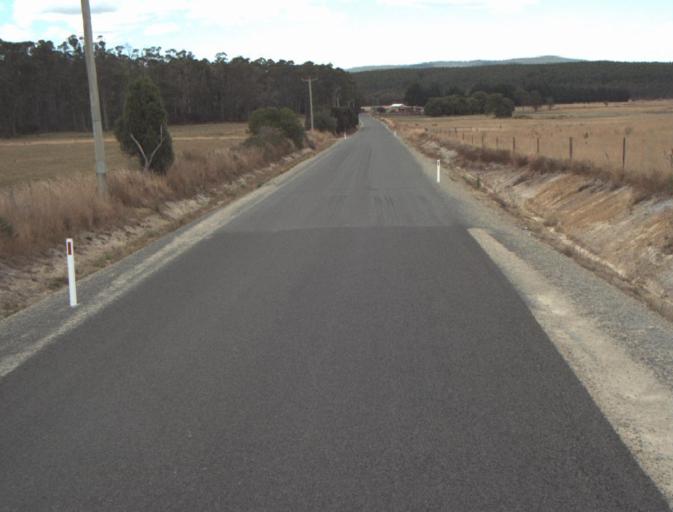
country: AU
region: Tasmania
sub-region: Launceston
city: Mayfield
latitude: -41.2022
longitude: 147.1892
